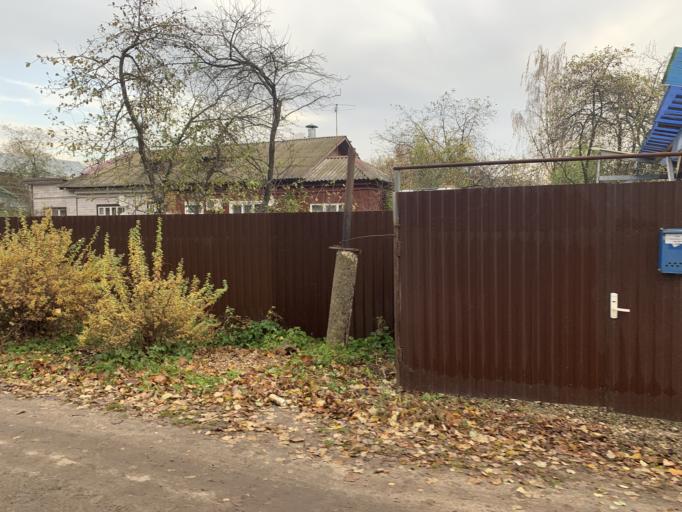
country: RU
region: Moskovskaya
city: Lesnyye Polyany
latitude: 55.9881
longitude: 37.8504
